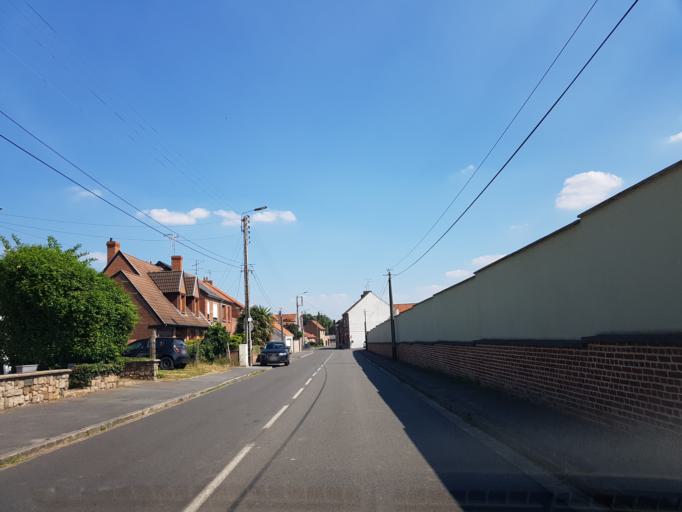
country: FR
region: Nord-Pas-de-Calais
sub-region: Departement du Nord
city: Roeulx
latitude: 50.3123
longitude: 3.3338
